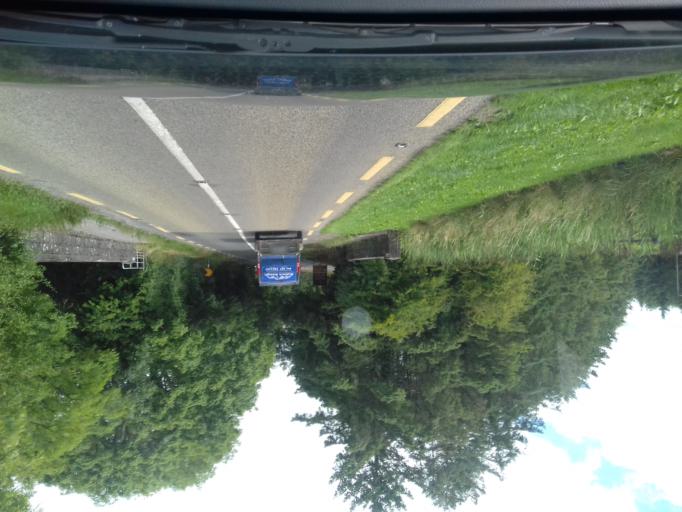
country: IE
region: Leinster
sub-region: Wicklow
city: Baltinglass
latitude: 52.9105
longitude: -6.6975
